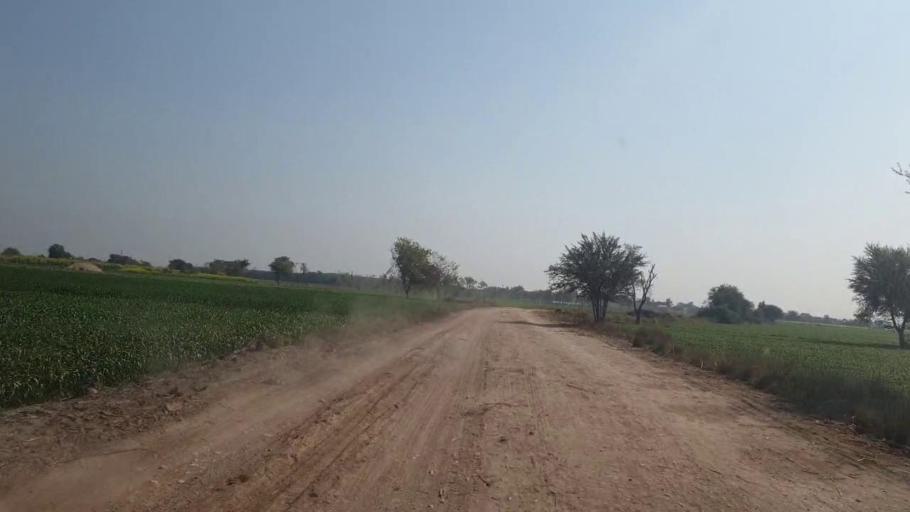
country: PK
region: Sindh
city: Sakrand
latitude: 26.0497
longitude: 68.4530
